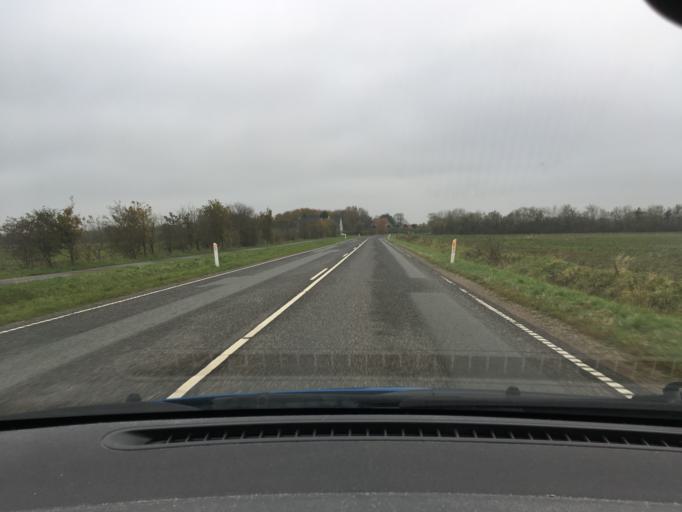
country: DK
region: South Denmark
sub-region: Aabenraa Kommune
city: Rodekro
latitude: 55.0723
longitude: 9.1988
